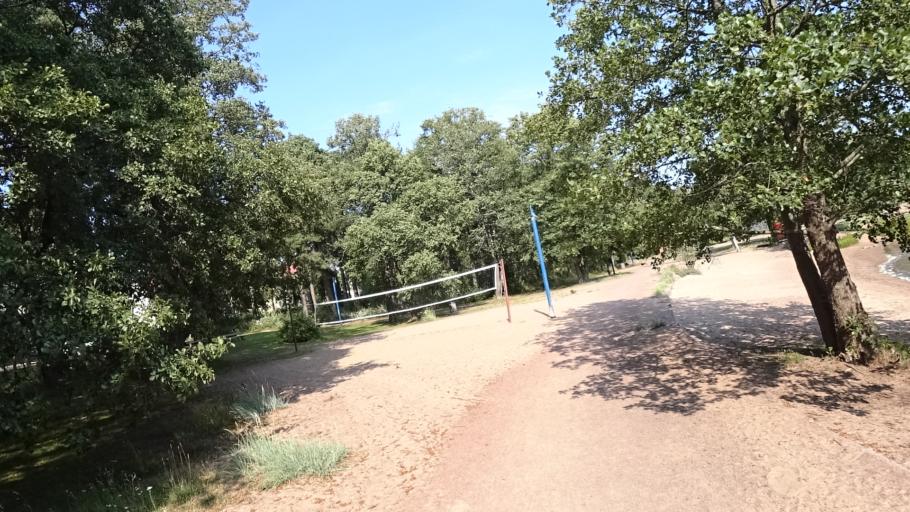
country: FI
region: Kymenlaakso
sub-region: Kotka-Hamina
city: Kotka
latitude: 60.4510
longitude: 26.9455
